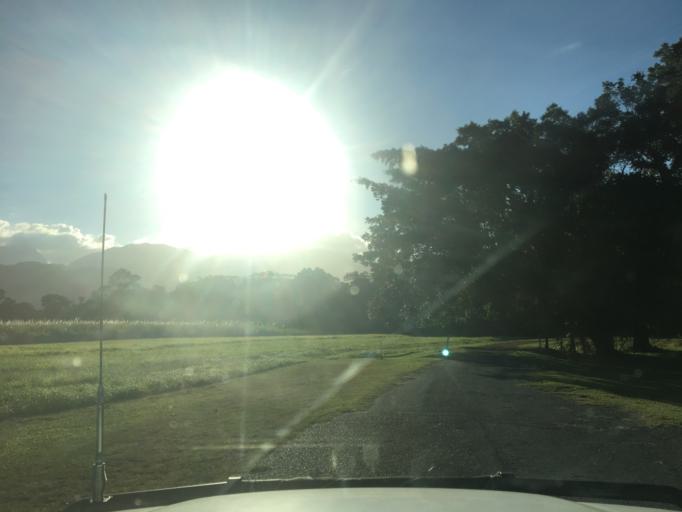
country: AU
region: Queensland
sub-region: Cairns
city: Port Douglas
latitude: -16.4547
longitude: 145.3712
